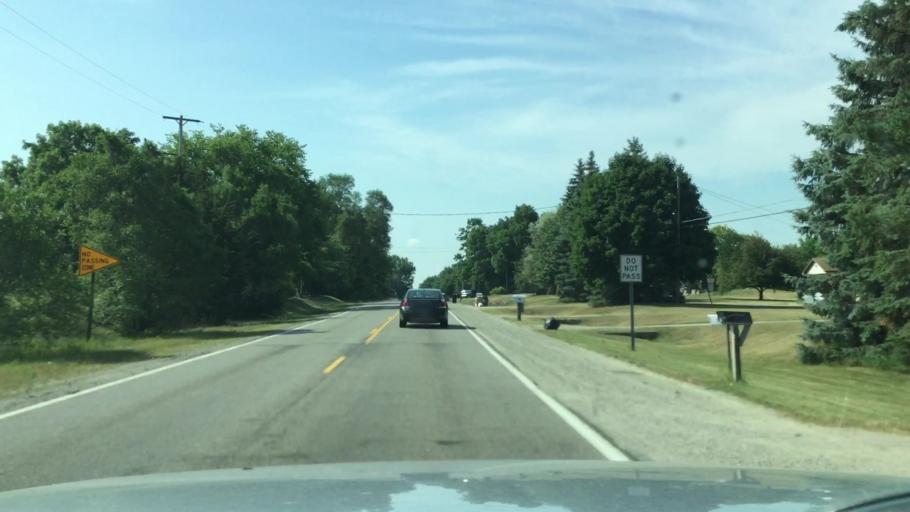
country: US
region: Michigan
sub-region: Genesee County
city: Flushing
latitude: 43.1028
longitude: -83.8137
